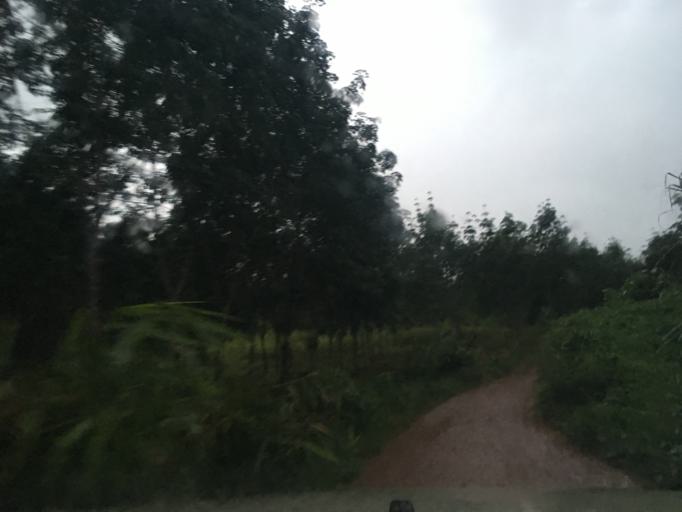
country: LA
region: Oudomxai
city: Muang La
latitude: 21.2502
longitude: 101.9325
